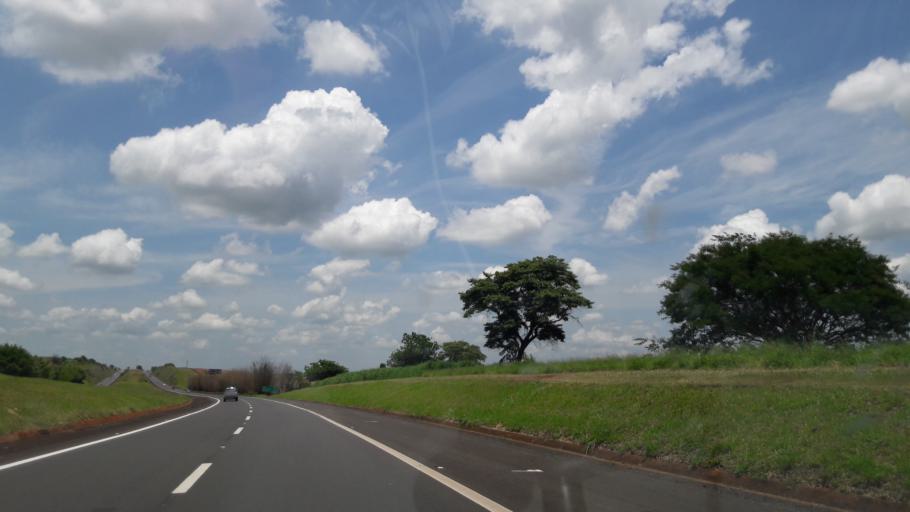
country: BR
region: Sao Paulo
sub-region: Avare
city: Avare
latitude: -22.9543
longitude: -48.8266
